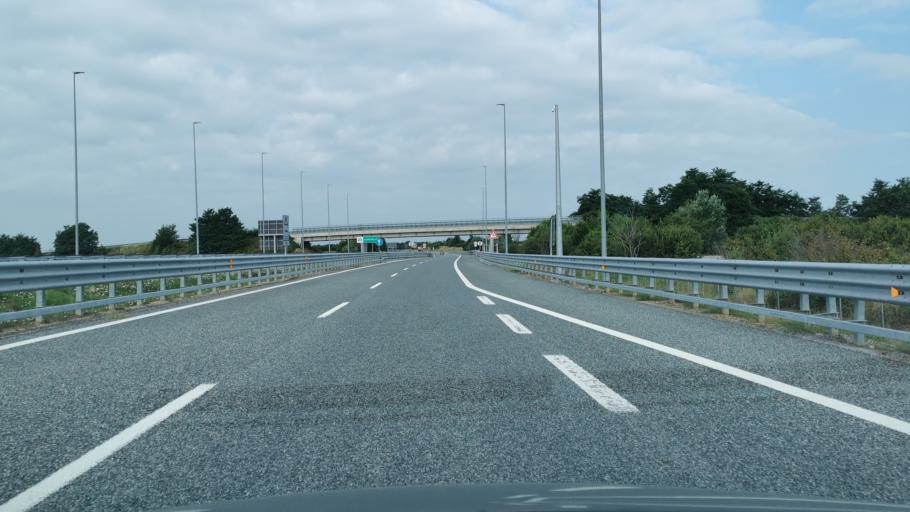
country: IT
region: Piedmont
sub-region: Provincia di Cuneo
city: Magliano Alpi
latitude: 44.4850
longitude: 7.8118
